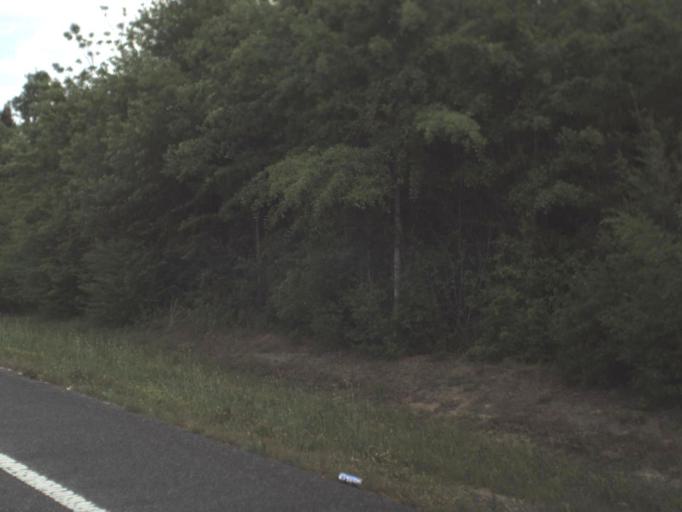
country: US
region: Florida
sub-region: Santa Rosa County
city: Wallace
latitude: 30.8153
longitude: -87.1319
